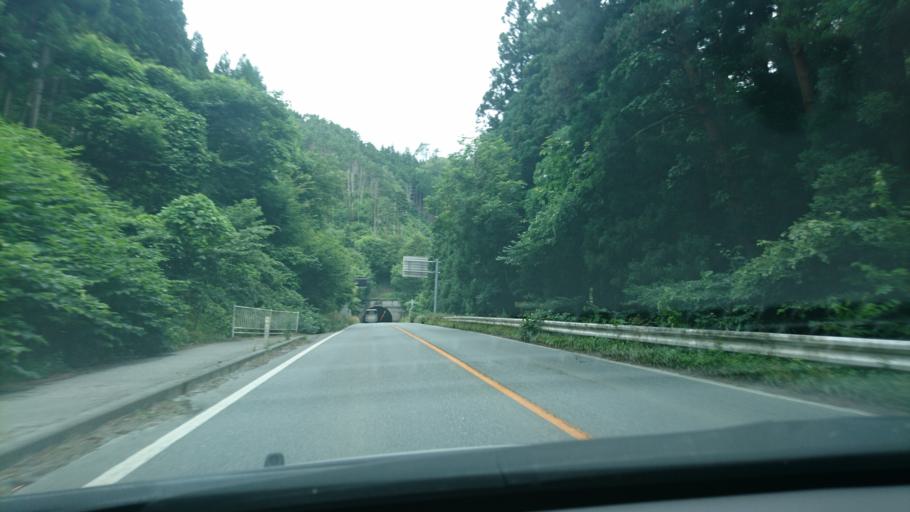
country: JP
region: Iwate
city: Otsuchi
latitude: 39.3427
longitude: 141.8934
